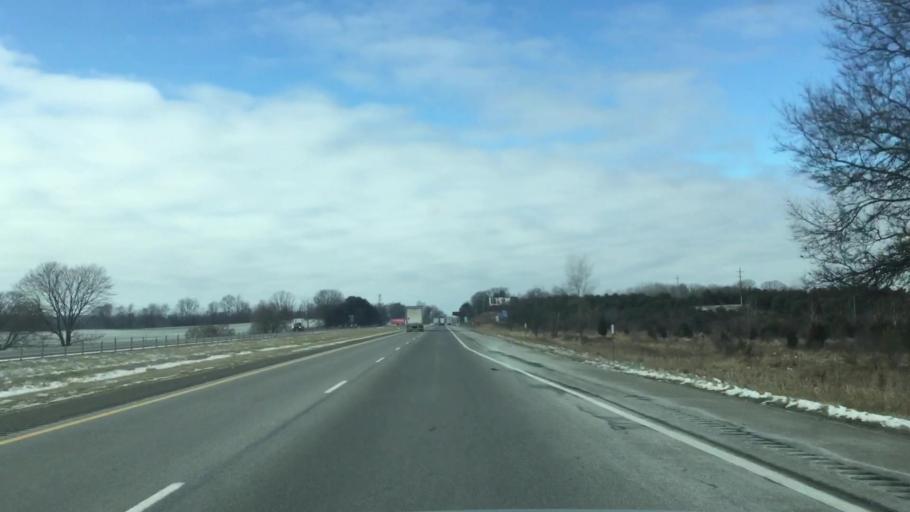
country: US
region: Michigan
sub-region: Calhoun County
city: Lakeview
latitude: 42.2660
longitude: -85.2453
